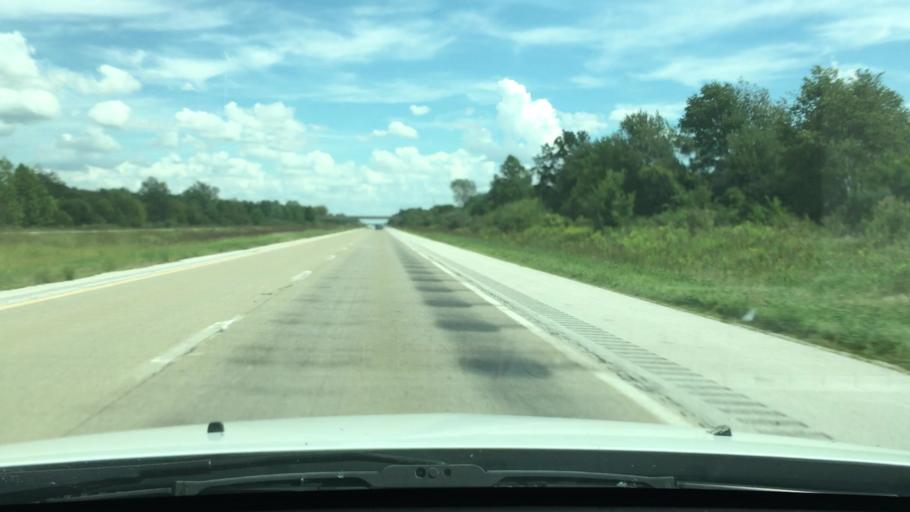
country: US
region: Illinois
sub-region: Scott County
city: Winchester
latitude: 39.6808
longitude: -90.5138
